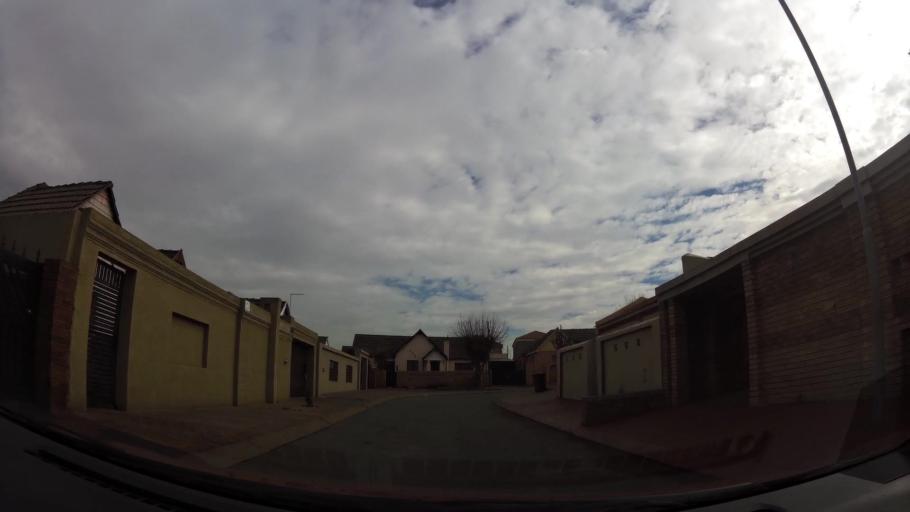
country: ZA
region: Gauteng
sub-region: City of Johannesburg Metropolitan Municipality
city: Soweto
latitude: -26.2780
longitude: 27.8321
